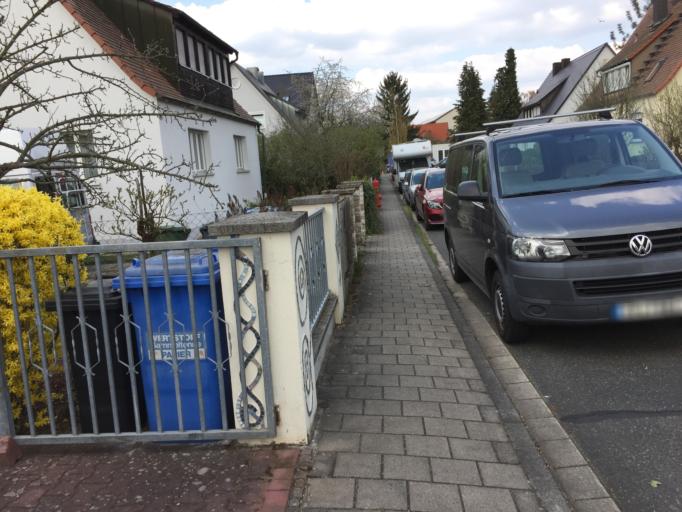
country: DE
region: Bavaria
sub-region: Regierungsbezirk Mittelfranken
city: Erlangen
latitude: 49.5656
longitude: 10.9990
